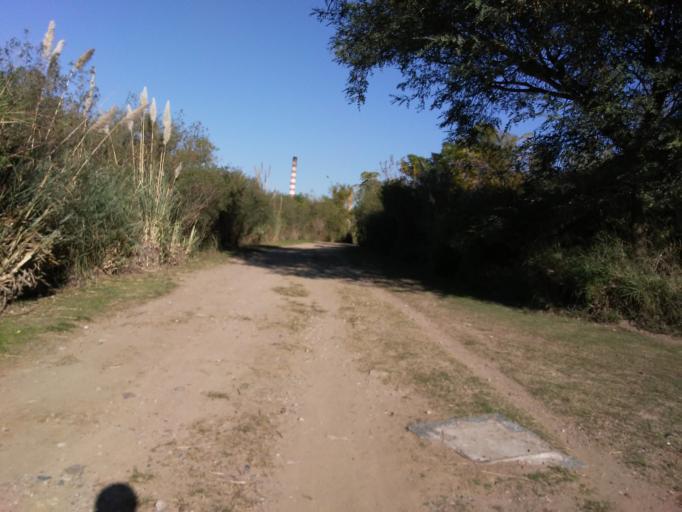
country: AR
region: Buenos Aires F.D.
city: Buenos Aires
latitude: -34.6154
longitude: -58.3402
